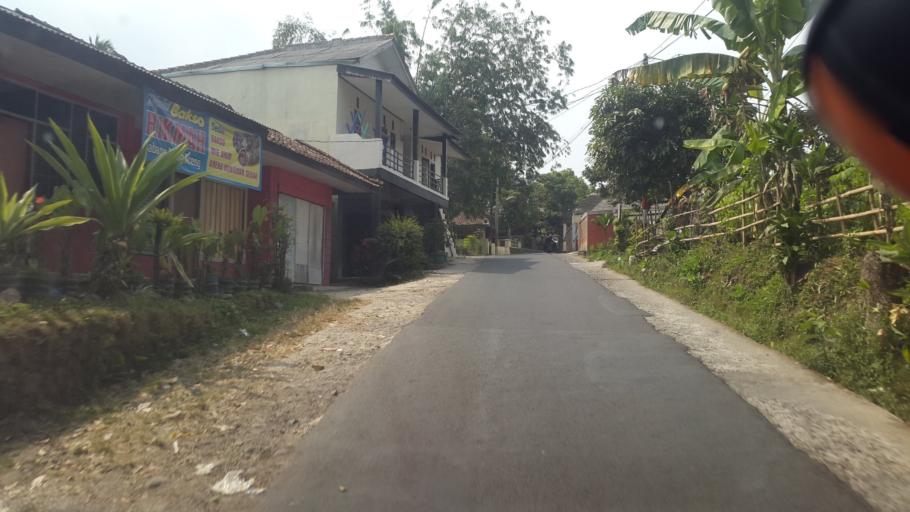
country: ID
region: West Java
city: Cicurug
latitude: -6.7583
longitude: 106.7731
